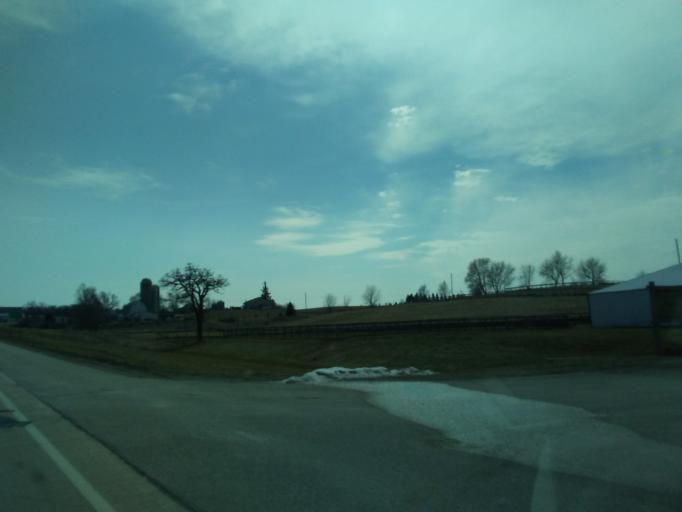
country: US
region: Minnesota
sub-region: Fillmore County
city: Preston
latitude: 43.6927
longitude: -92.0989
